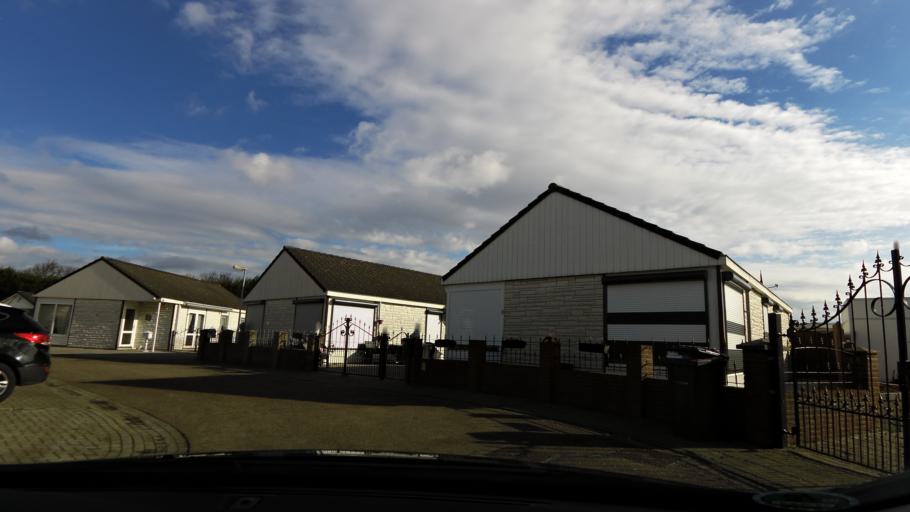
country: NL
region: Limburg
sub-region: Gemeente Voerendaal
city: Klimmen
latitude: 50.8806
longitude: 5.8781
